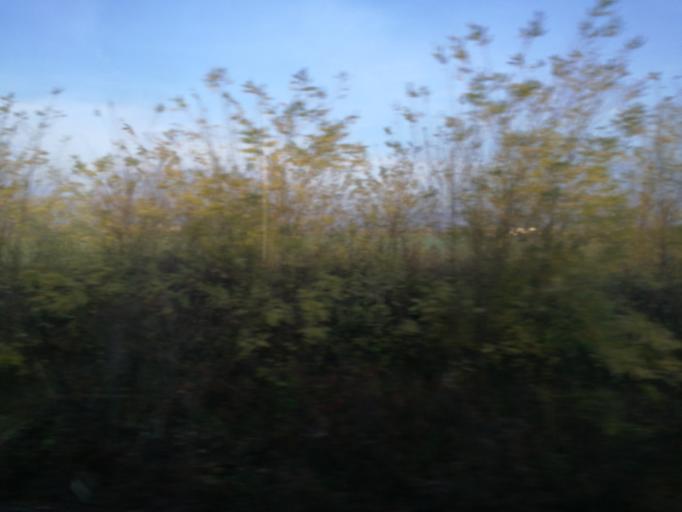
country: RO
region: Buzau
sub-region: Comuna Stalpu
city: Stalpu
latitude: 45.0959
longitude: 26.6897
